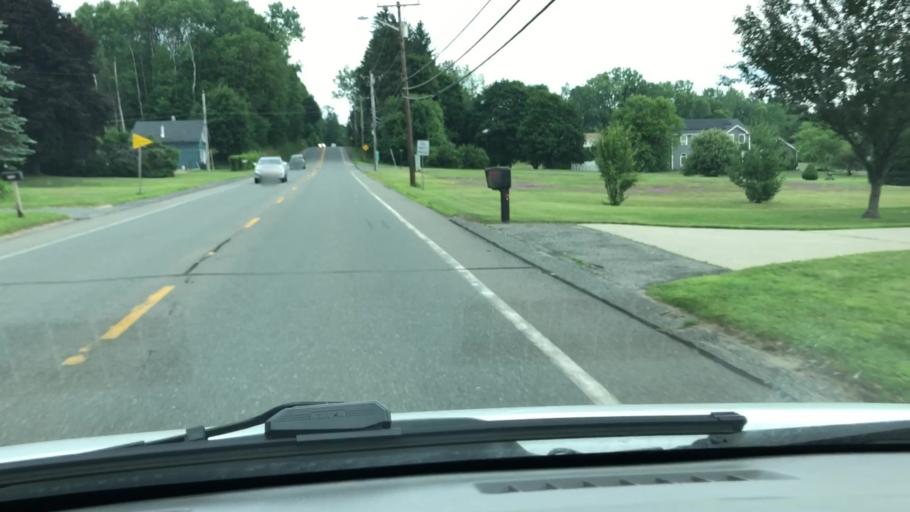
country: US
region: Massachusetts
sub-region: Berkshire County
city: Adams
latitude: 42.5727
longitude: -73.1539
